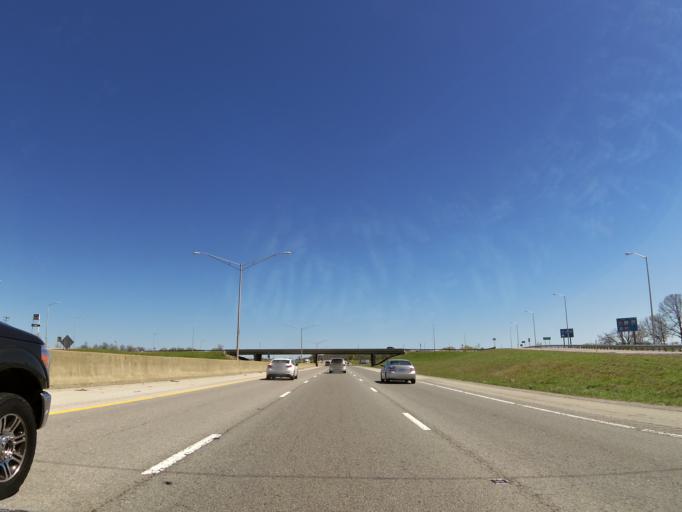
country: US
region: Kentucky
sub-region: Edmonson County
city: Brownsville
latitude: 37.0422
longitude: -86.2125
